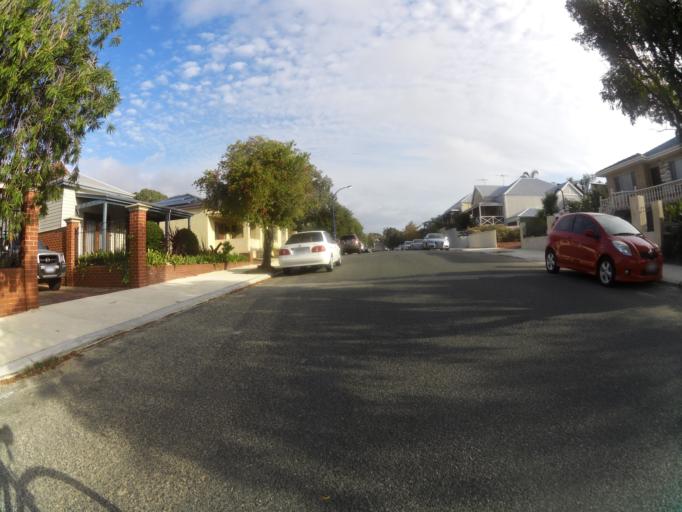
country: AU
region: Western Australia
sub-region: East Fremantle
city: East Fremantle
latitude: -32.0429
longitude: 115.7591
